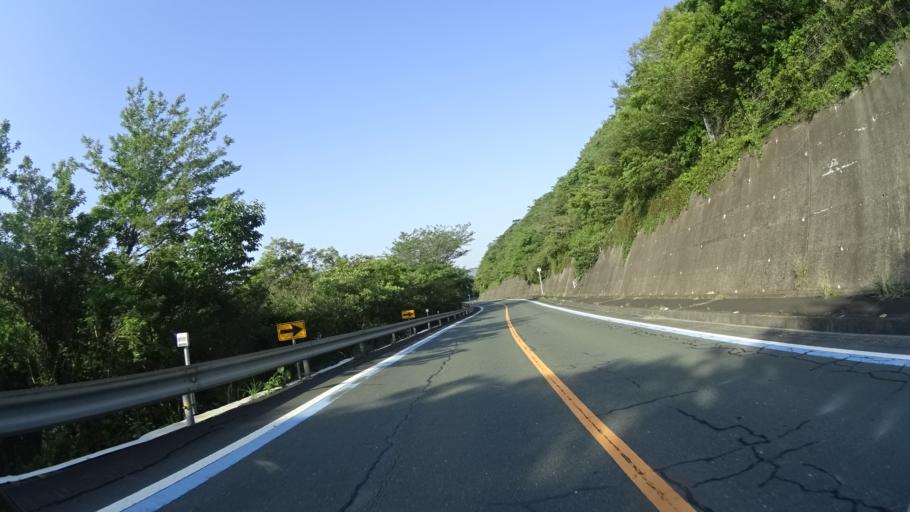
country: JP
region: Ehime
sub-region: Nishiuwa-gun
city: Ikata-cho
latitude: 33.4666
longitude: 132.2758
